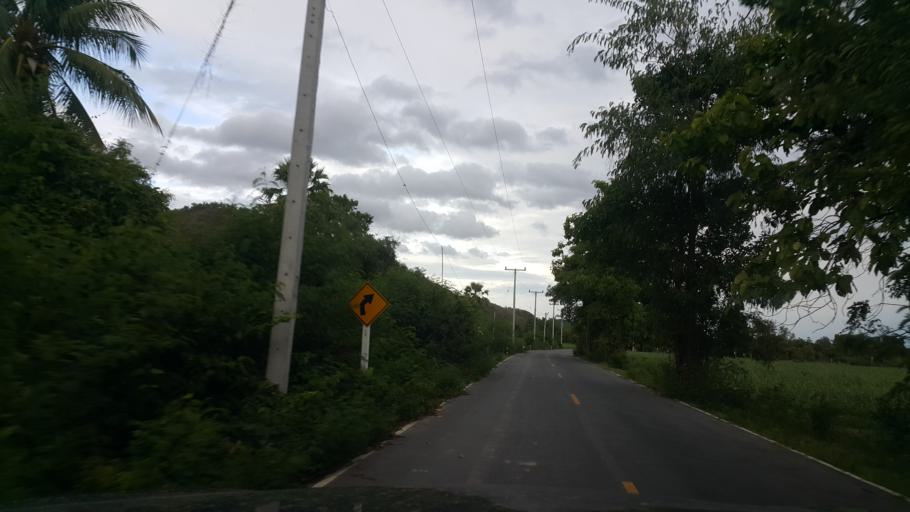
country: TH
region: Sukhothai
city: Thung Saliam
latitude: 17.1637
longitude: 99.4984
